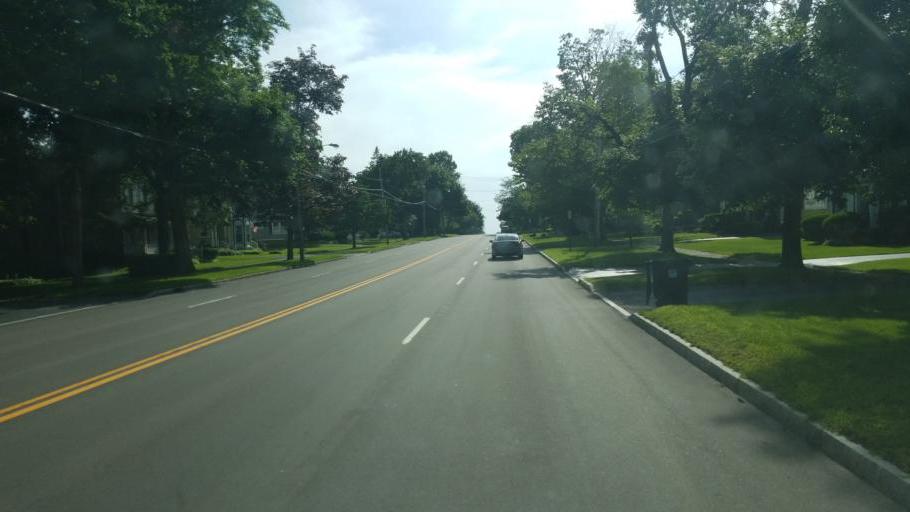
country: US
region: New York
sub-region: Genesee County
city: Le Roy
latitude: 42.9793
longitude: -77.9790
